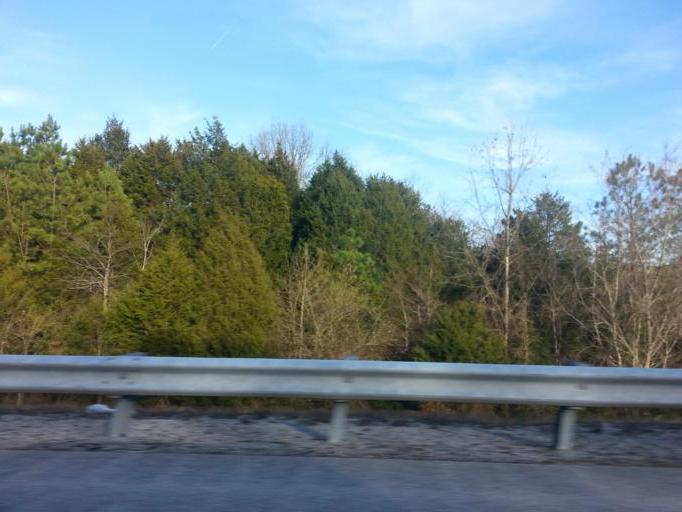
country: US
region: Tennessee
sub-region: White County
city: Sparta
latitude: 35.9044
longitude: -85.4722
